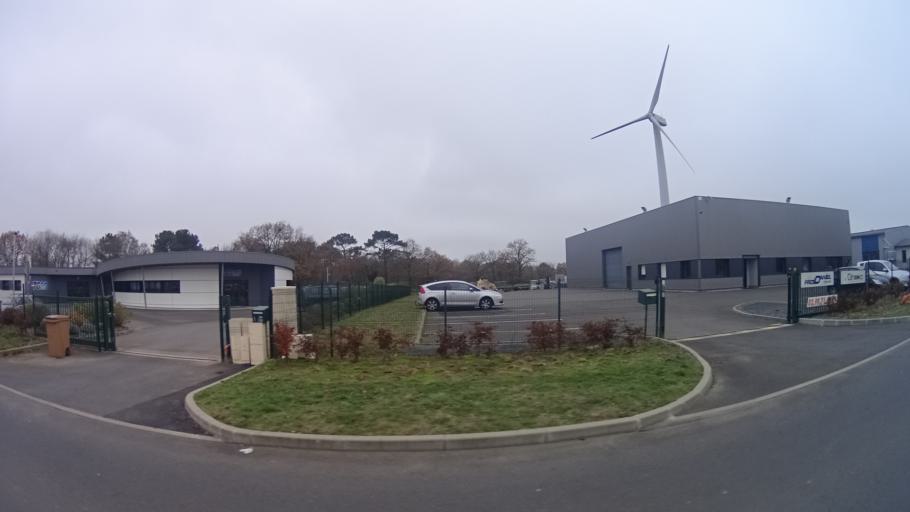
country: FR
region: Brittany
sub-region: Departement d'Ille-et-Vilaine
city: Bains-sur-Oust
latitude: 47.6819
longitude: -2.0527
